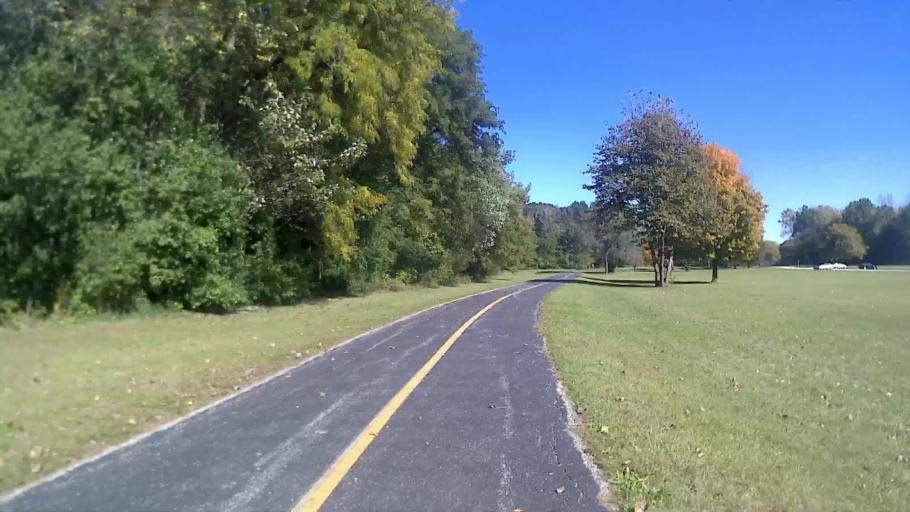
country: US
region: Illinois
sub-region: DuPage County
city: Itasca
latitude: 42.0172
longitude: -88.0163
